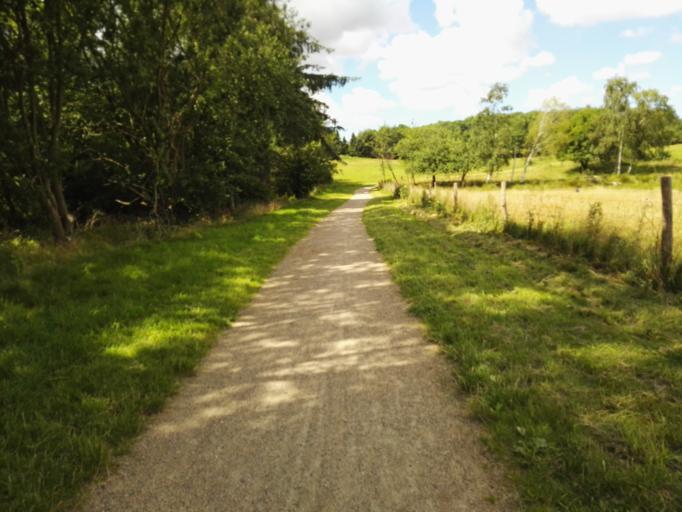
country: DK
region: Capital Region
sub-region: Ballerup Kommune
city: Ballerup
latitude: 55.7506
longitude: 12.3546
